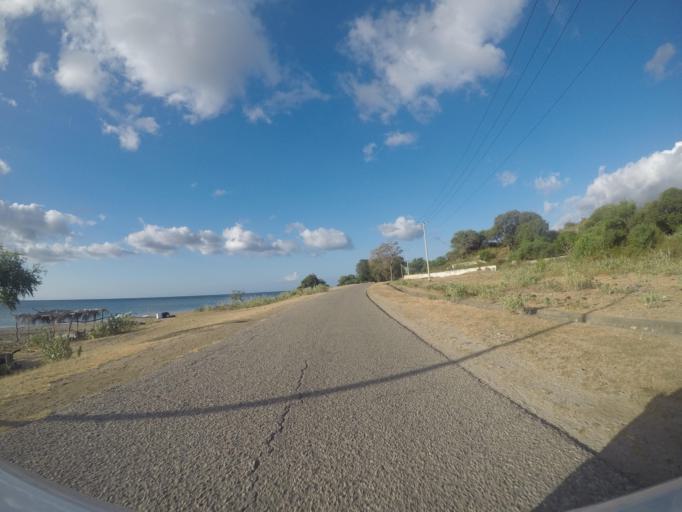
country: TL
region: Lautem
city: Lospalos
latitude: -8.3606
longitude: 126.9063
